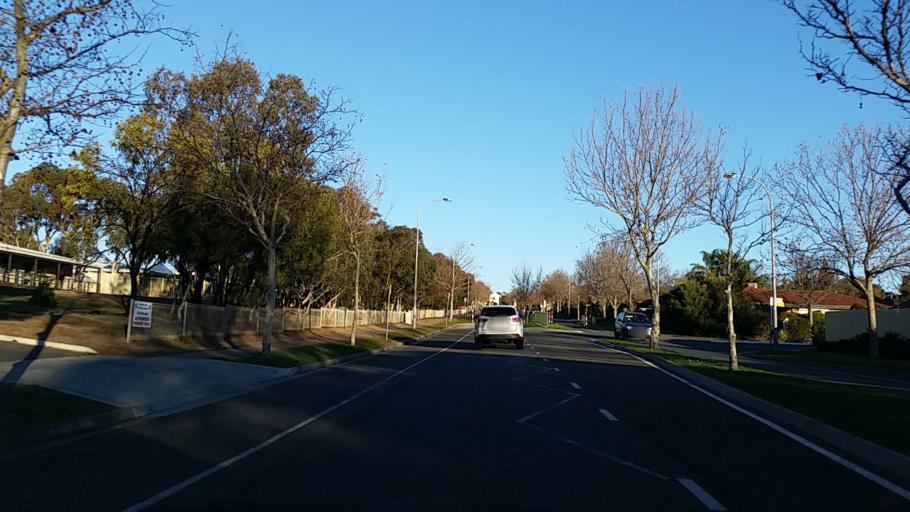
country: AU
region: South Australia
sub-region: Onkaparinga
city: Moana
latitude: -35.1989
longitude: 138.4861
